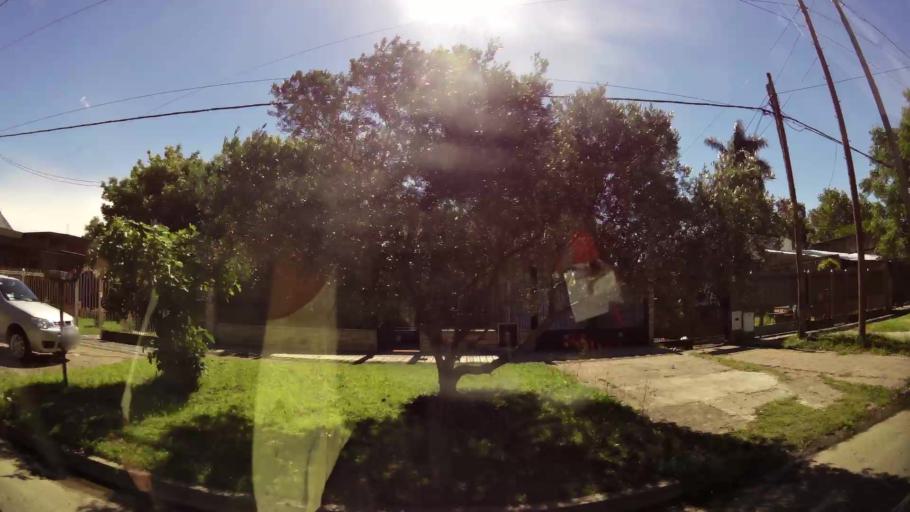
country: AR
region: Buenos Aires
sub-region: Partido de Almirante Brown
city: Adrogue
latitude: -34.7948
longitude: -58.3638
